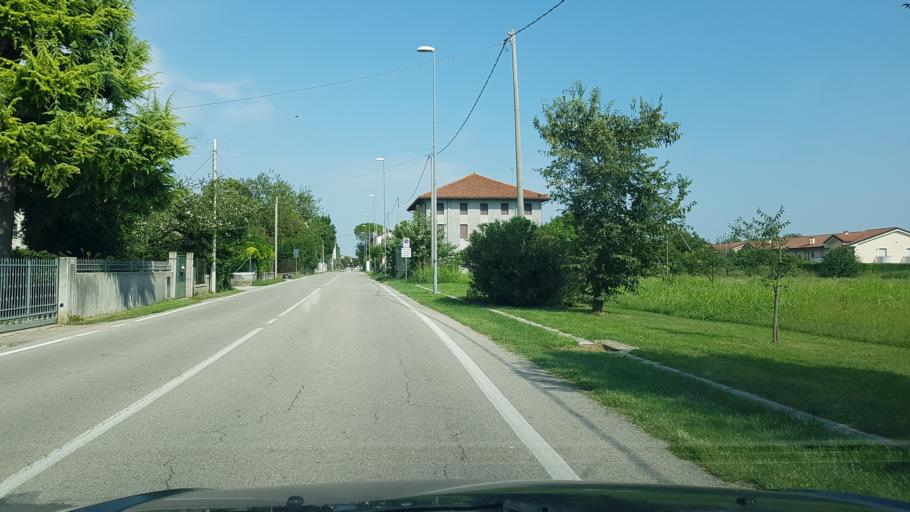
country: IT
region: Friuli Venezia Giulia
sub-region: Provincia di Pordenone
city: San Quirino
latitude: 46.0532
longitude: 12.6630
